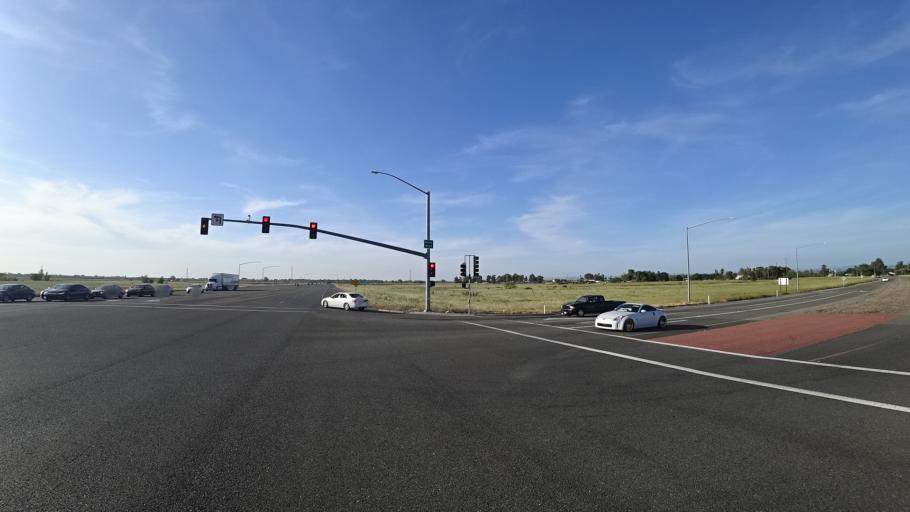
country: US
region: California
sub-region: Placer County
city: Sheridan
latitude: 38.9789
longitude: -121.3824
